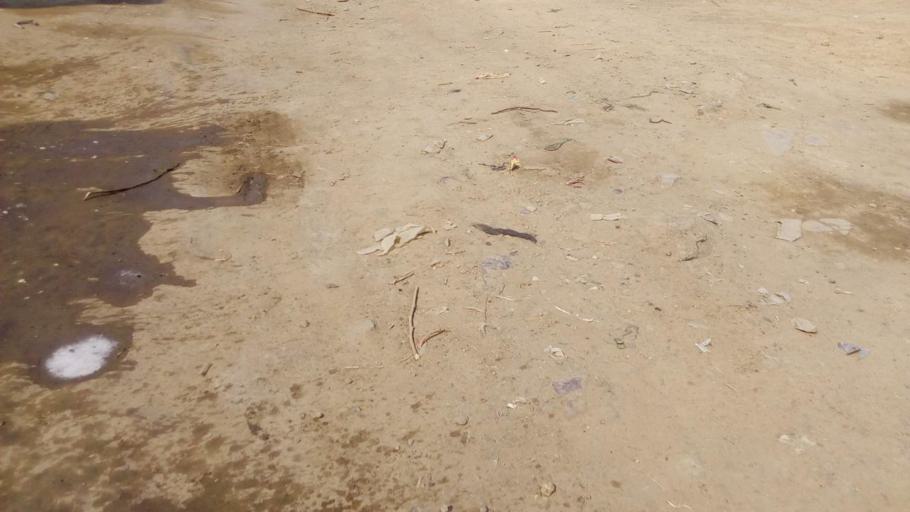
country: ZM
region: Lusaka
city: Lusaka
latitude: -15.3575
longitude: 28.2873
